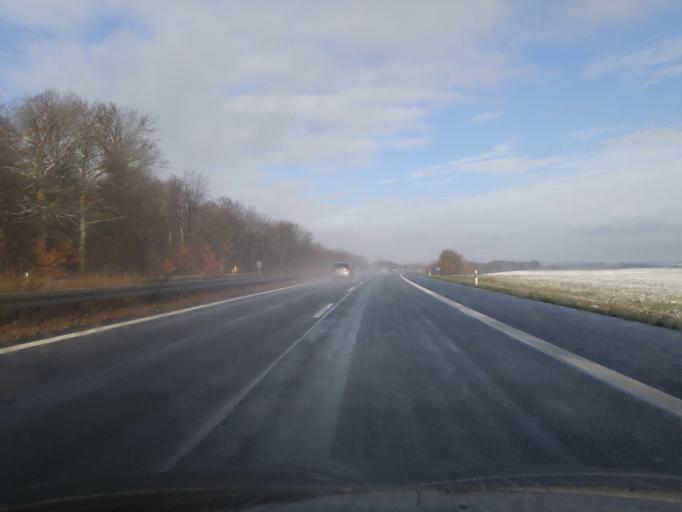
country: DE
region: Bavaria
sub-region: Regierungsbezirk Unterfranken
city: Arnstein
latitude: 49.9293
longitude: 9.9992
